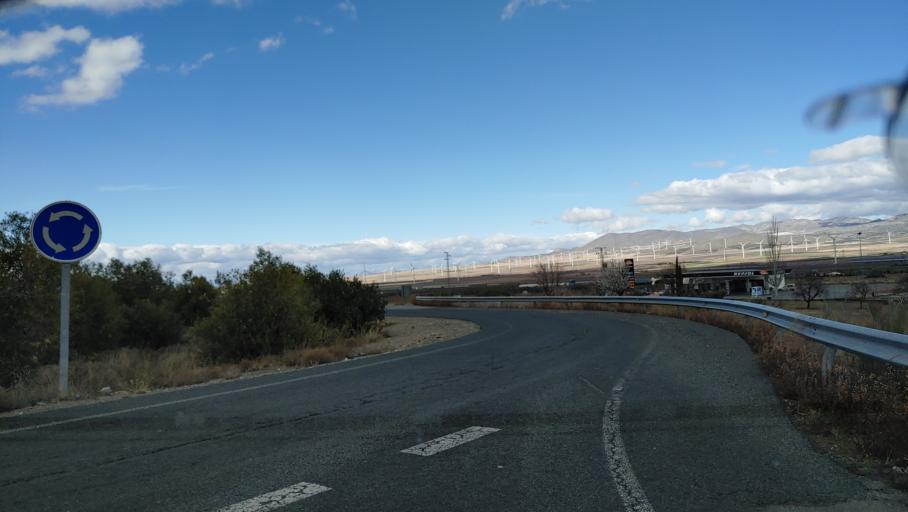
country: ES
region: Andalusia
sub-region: Provincia de Granada
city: Hueneja
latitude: 37.1875
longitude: -2.9547
